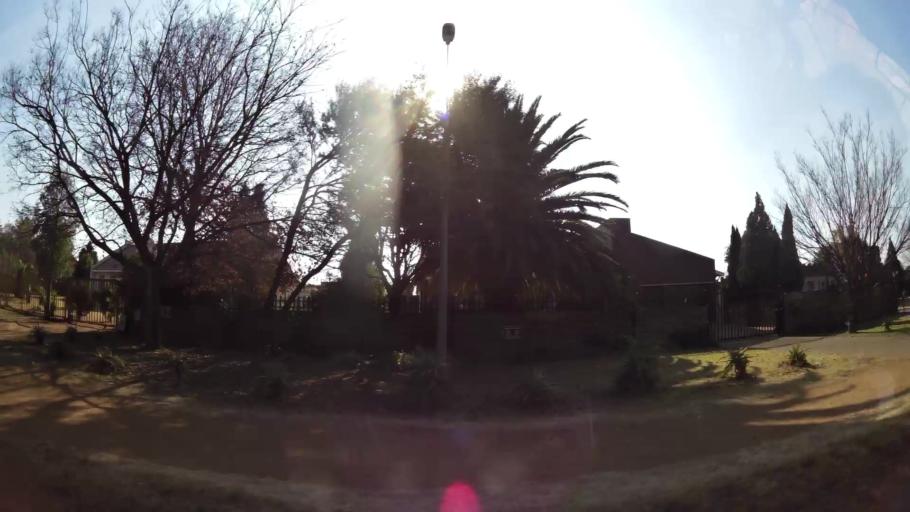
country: ZA
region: Gauteng
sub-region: West Rand District Municipality
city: Randfontein
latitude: -26.1847
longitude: 27.6839
